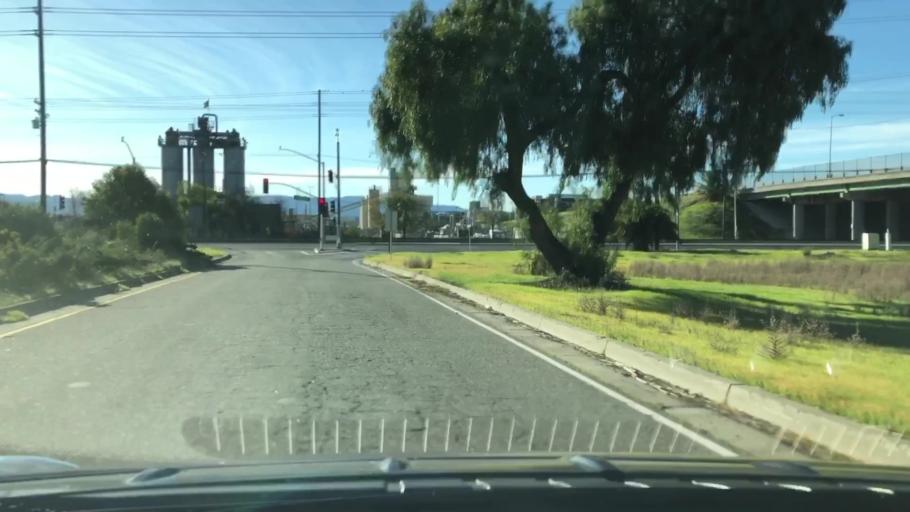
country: US
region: California
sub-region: Santa Clara County
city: Santa Clara
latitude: 37.3890
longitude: -121.9536
